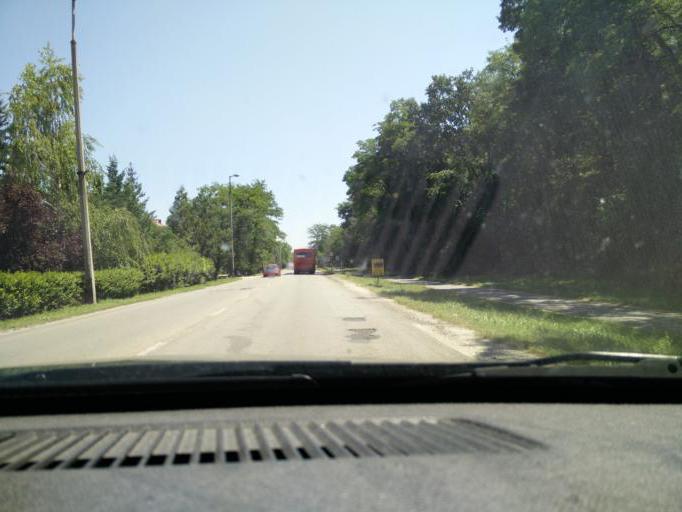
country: HU
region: Komarom-Esztergom
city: Baj
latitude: 47.6411
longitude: 18.3427
